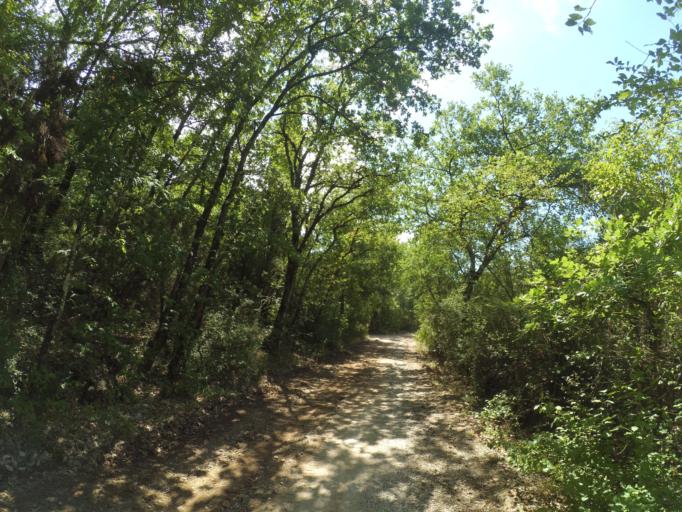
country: IT
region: Tuscany
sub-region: Province of Arezzo
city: Castiglion Fibocchi
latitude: 43.5408
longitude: 11.7678
